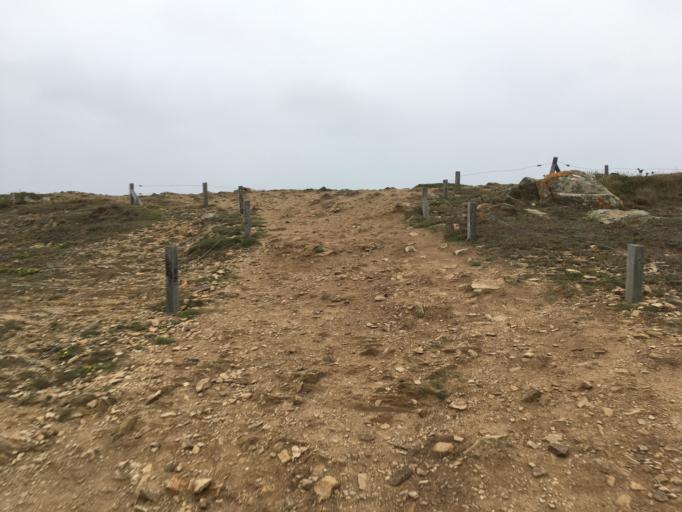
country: FR
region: Brittany
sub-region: Departement du Finistere
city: Plogoff
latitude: 48.0537
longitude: -4.7129
